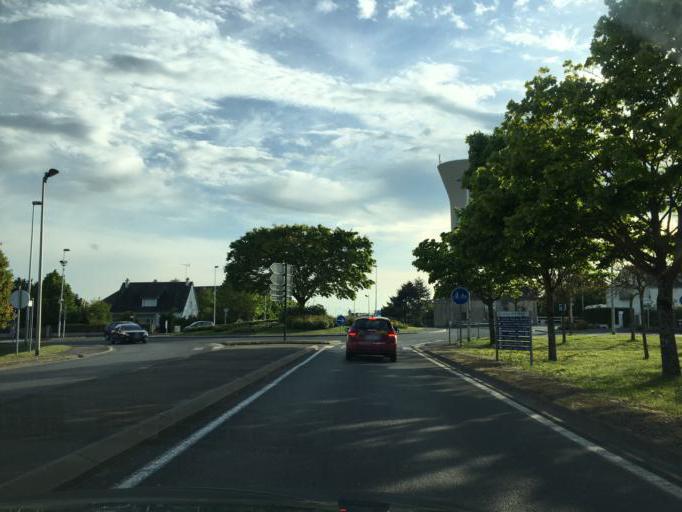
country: FR
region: Centre
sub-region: Departement du Loiret
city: Ormes
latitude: 47.9439
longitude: 1.8168
